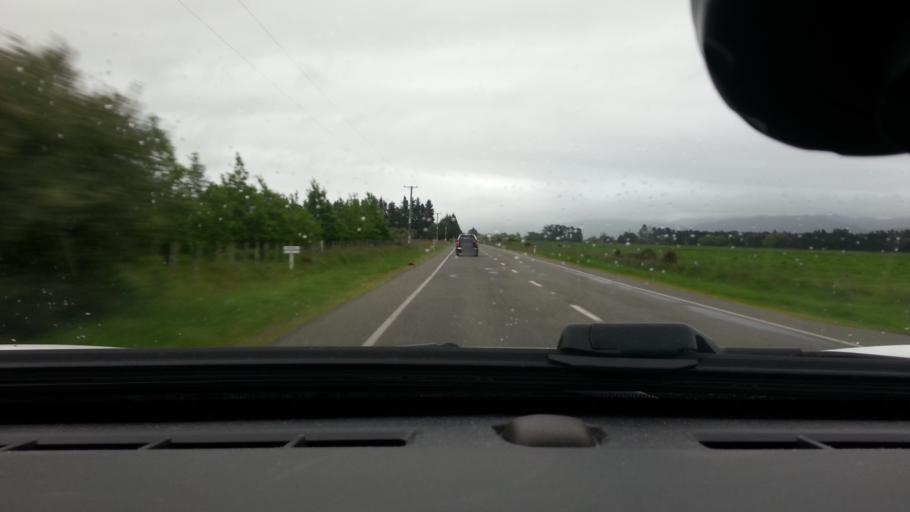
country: NZ
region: Wellington
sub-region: Masterton District
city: Masterton
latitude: -41.1089
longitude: 175.4022
